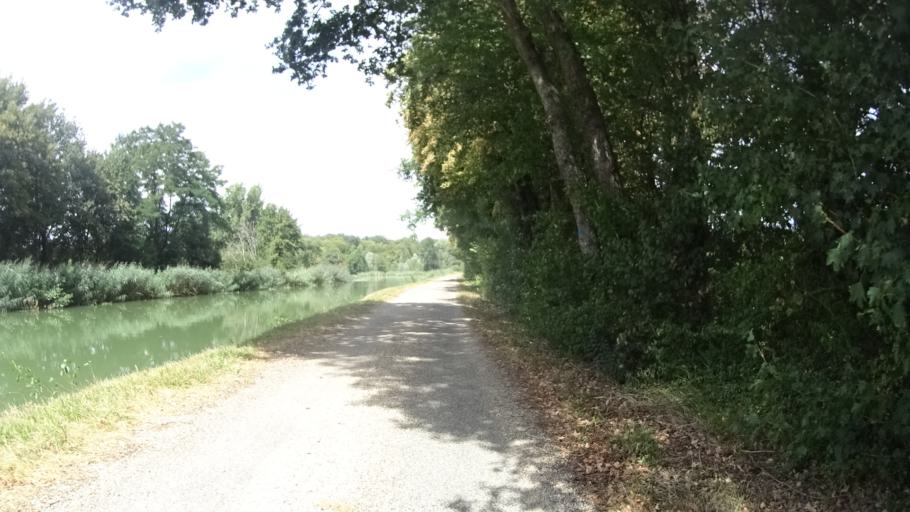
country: FR
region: Bourgogne
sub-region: Departement de la Cote-d'Or
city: Saint-Jean-de-Losne
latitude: 47.0945
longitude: 5.3248
